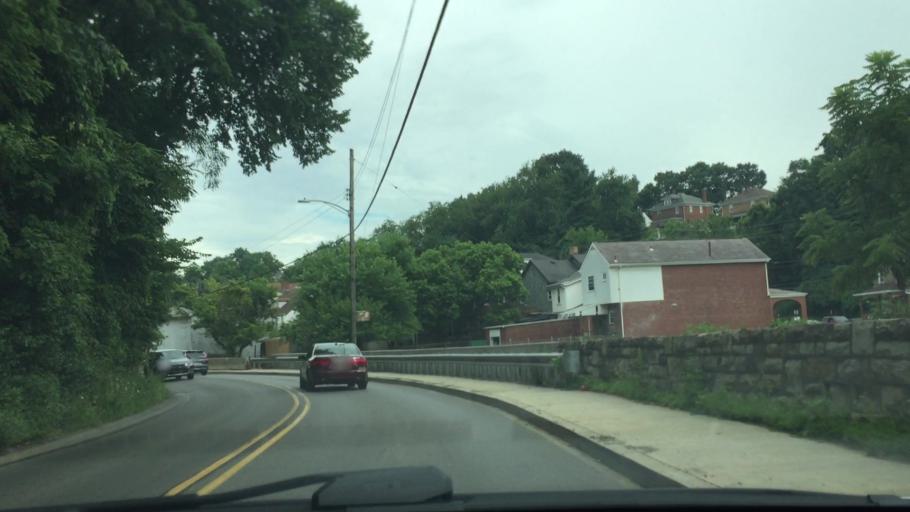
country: US
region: Pennsylvania
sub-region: Allegheny County
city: Bridgeville
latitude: 40.3586
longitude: -80.1084
